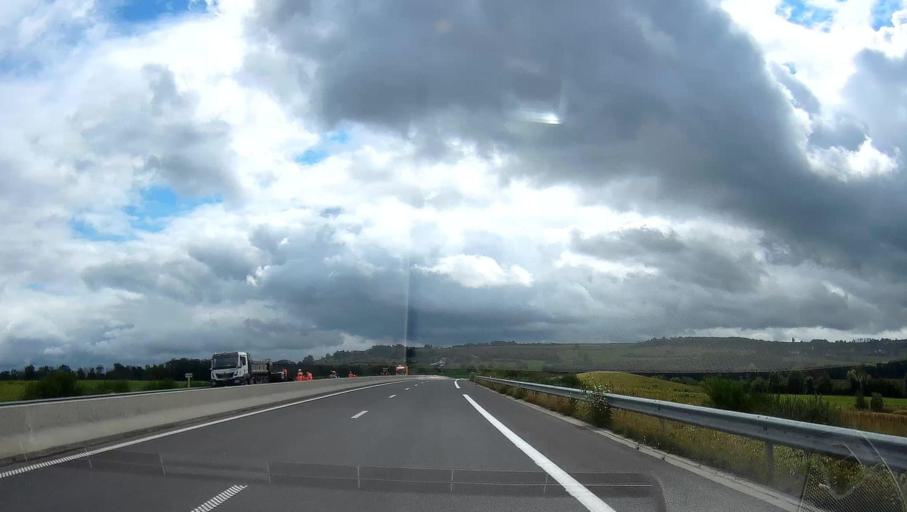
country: FR
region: Champagne-Ardenne
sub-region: Departement des Ardennes
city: Rimogne
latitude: 49.8016
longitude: 4.5323
